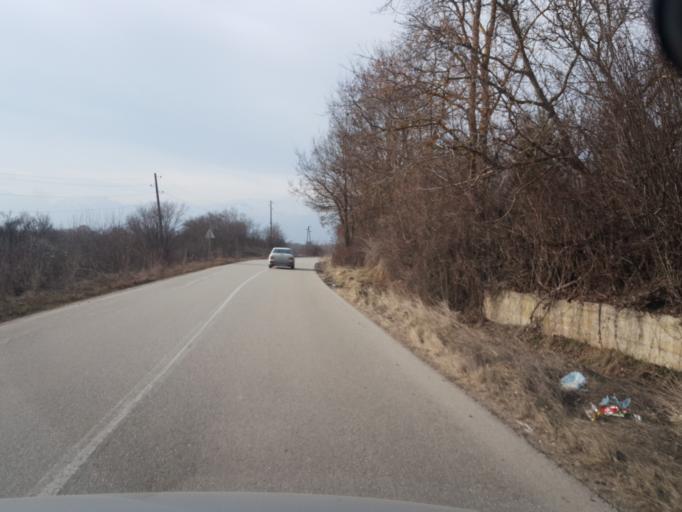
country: XK
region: Pec
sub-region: Komuna e Klines
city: Klina
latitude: 42.6760
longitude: 20.5273
